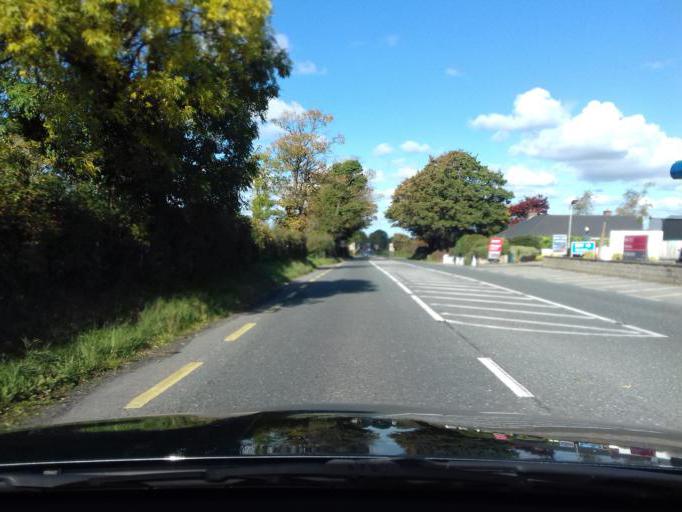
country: IE
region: Leinster
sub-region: An Mhi
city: Ratoath
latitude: 53.5527
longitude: -6.4360
